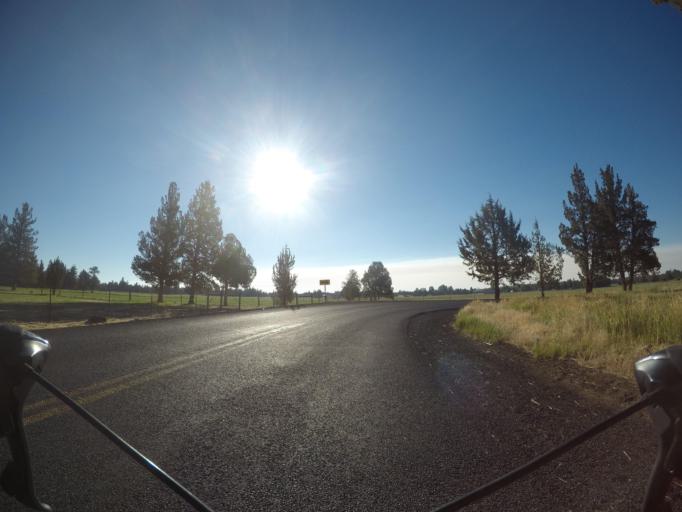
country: US
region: Oregon
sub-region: Deschutes County
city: Redmond
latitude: 44.2657
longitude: -121.2456
